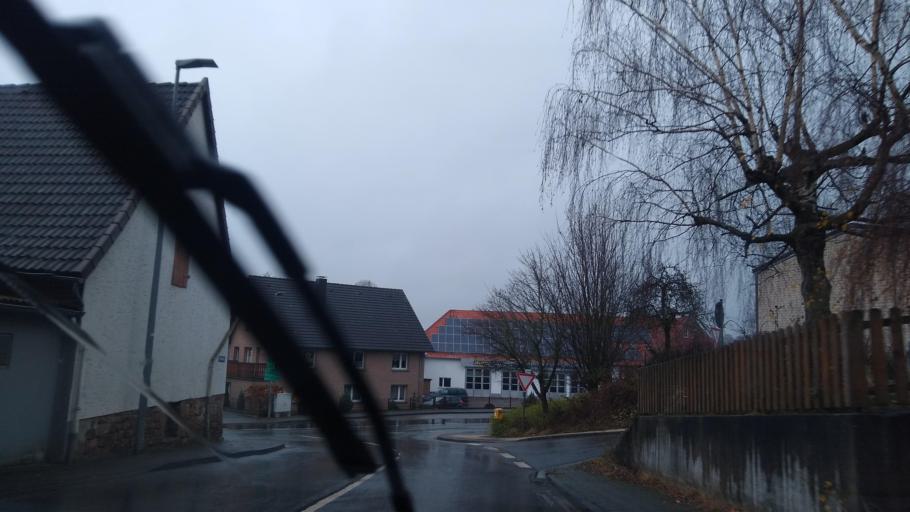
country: DE
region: North Rhine-Westphalia
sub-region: Regierungsbezirk Detmold
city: Lugde
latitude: 51.9099
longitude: 9.2529
